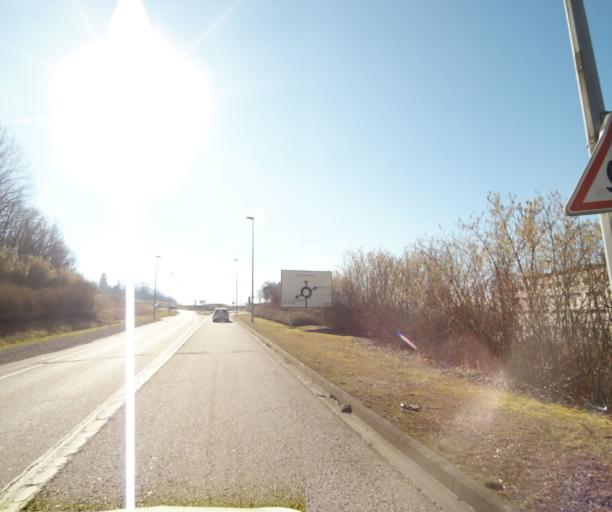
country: FR
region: Lorraine
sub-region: Departement de Meurthe-et-Moselle
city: Champigneulles
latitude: 48.7332
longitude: 6.1825
